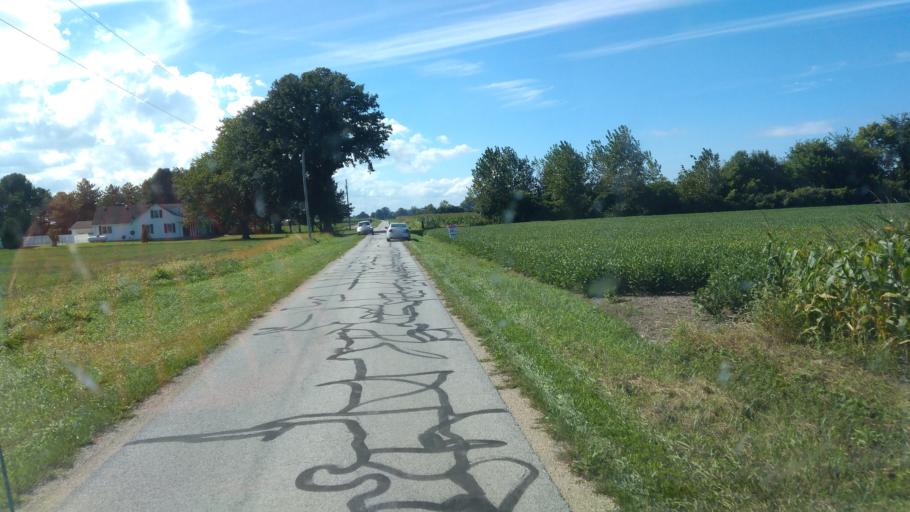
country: US
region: Ohio
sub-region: Ottawa County
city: Port Clinton
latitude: 41.4083
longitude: -82.8716
